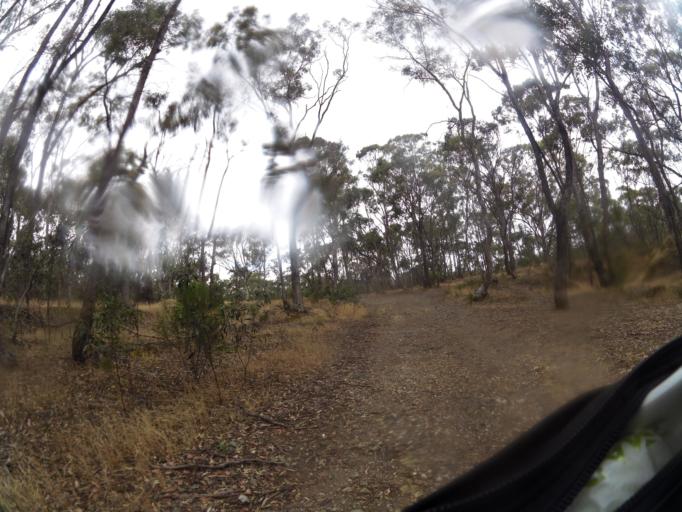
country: AU
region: Victoria
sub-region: Mount Alexander
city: Castlemaine
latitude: -37.0714
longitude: 144.2590
